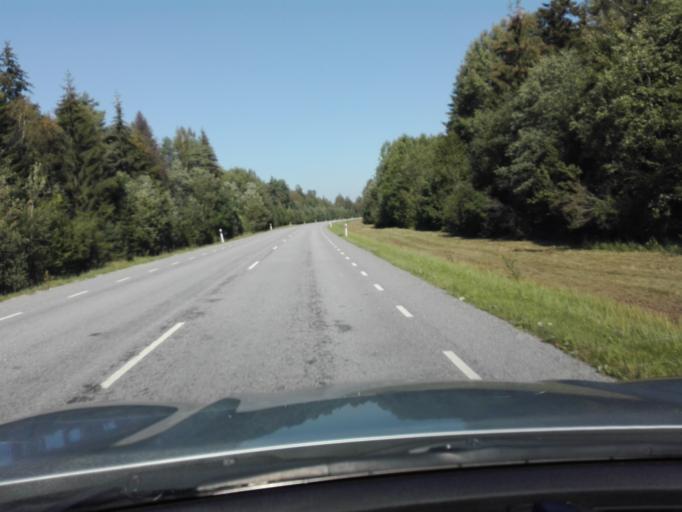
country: EE
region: Raplamaa
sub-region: Rapla vald
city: Rapla
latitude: 59.0078
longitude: 24.7698
